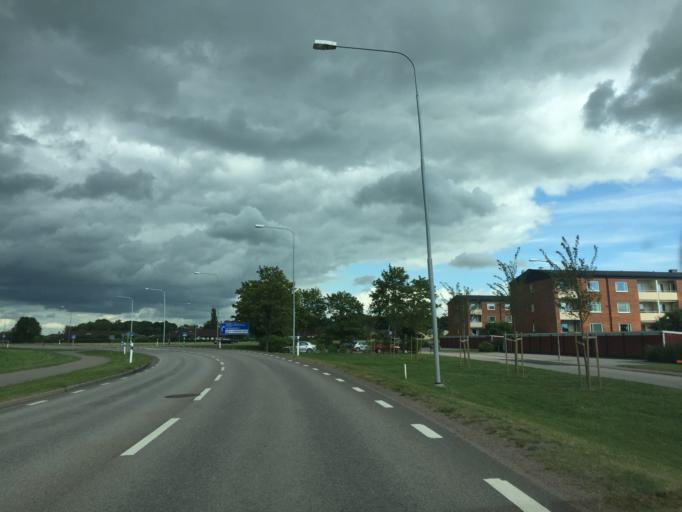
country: SE
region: OEstergoetland
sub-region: Vadstena Kommun
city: Vadstena
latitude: 58.4472
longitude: 14.9046
